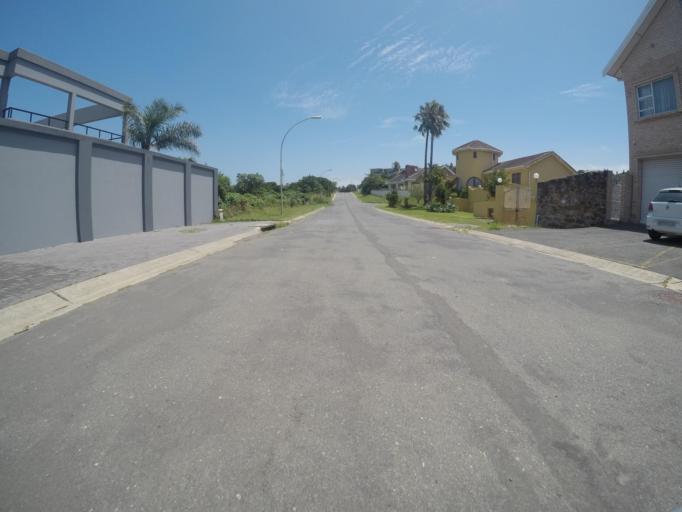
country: ZA
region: Eastern Cape
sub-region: Buffalo City Metropolitan Municipality
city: East London
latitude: -33.0044
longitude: 27.9225
